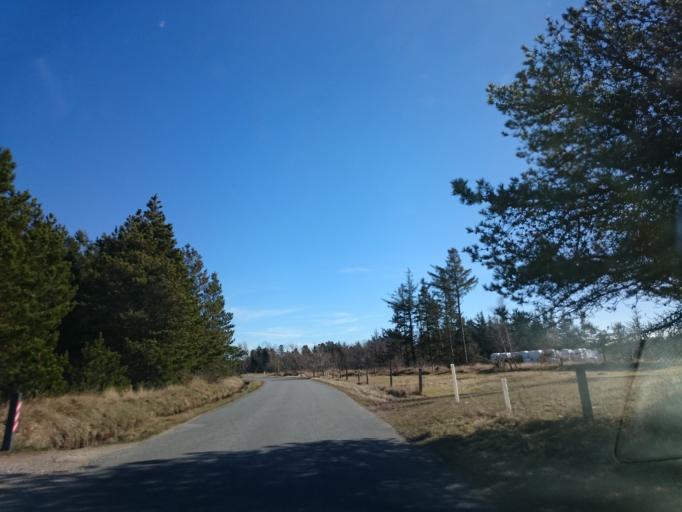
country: DK
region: North Denmark
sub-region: Frederikshavn Kommune
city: Strandby
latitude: 57.6270
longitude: 10.4016
